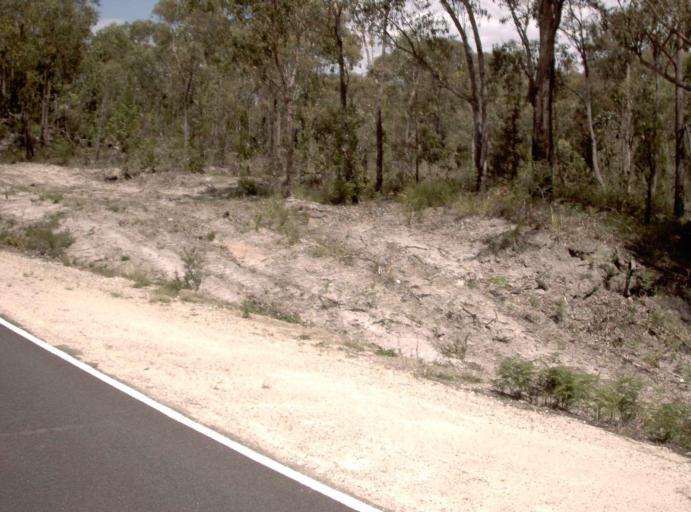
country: AU
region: New South Wales
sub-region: Bombala
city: Bombala
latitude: -37.5657
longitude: 149.2308
